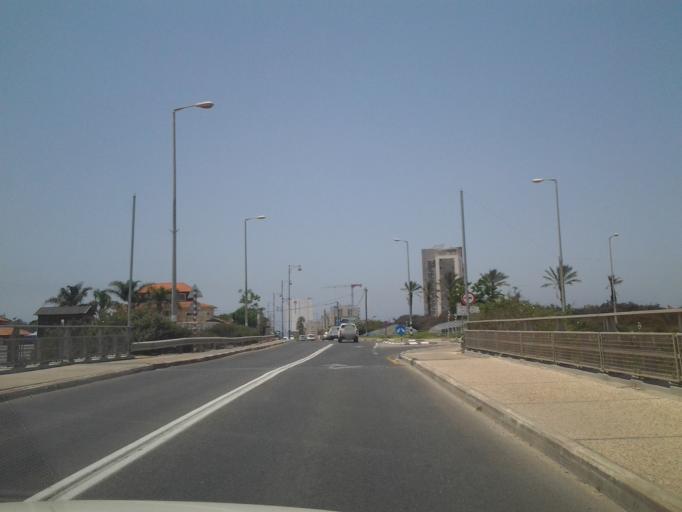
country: IL
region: Haifa
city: Hadera
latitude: 32.4438
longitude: 34.8925
